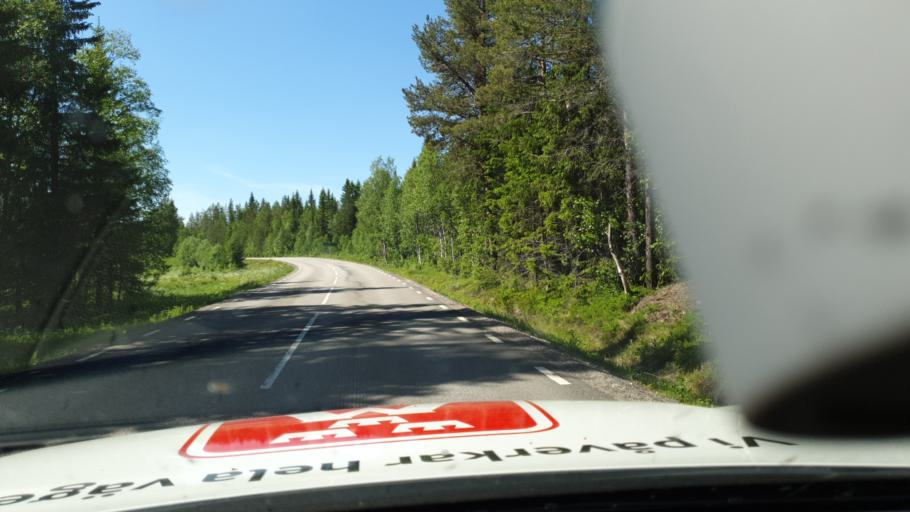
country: SE
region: Jaemtland
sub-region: Harjedalens Kommun
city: Sveg
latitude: 62.0992
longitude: 13.5787
